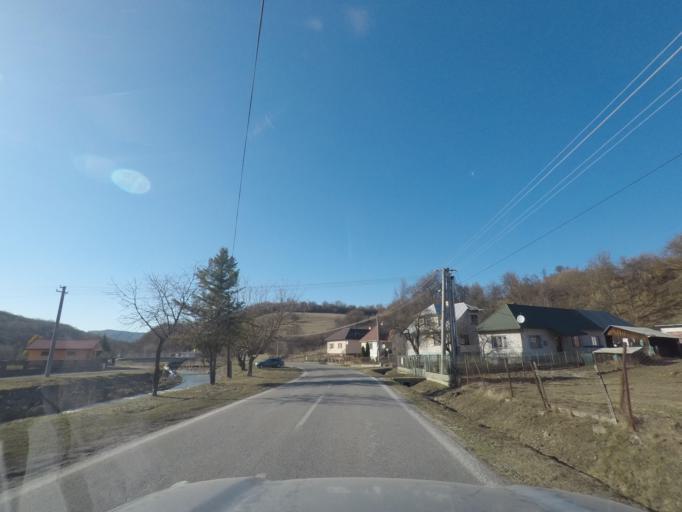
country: SK
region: Presovsky
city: Snina
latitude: 49.1203
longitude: 22.1346
